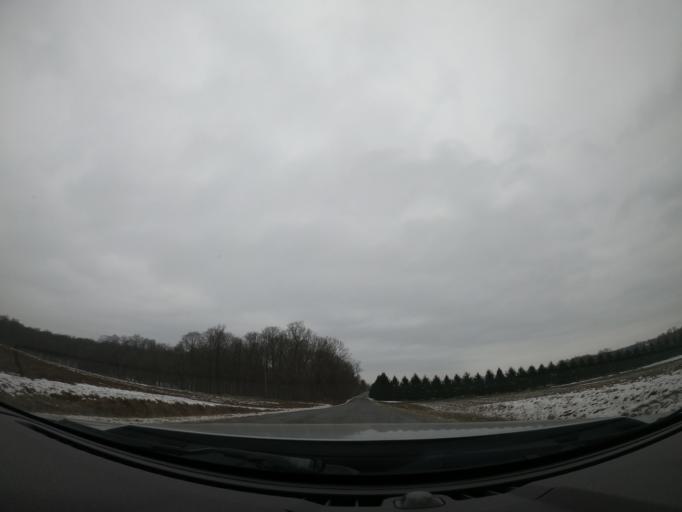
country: US
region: New York
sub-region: Cayuga County
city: Moravia
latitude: 42.6370
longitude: -76.4703
